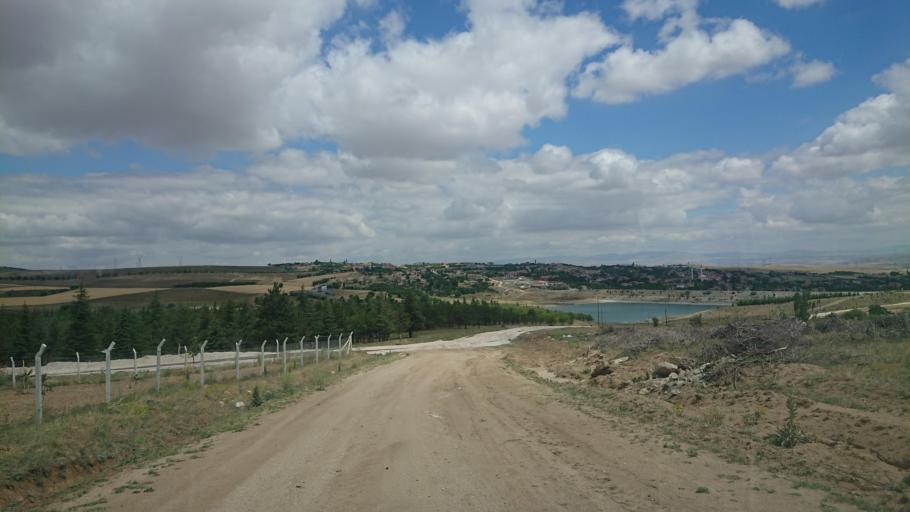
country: TR
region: Aksaray
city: Agacoren
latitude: 38.8590
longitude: 33.9481
